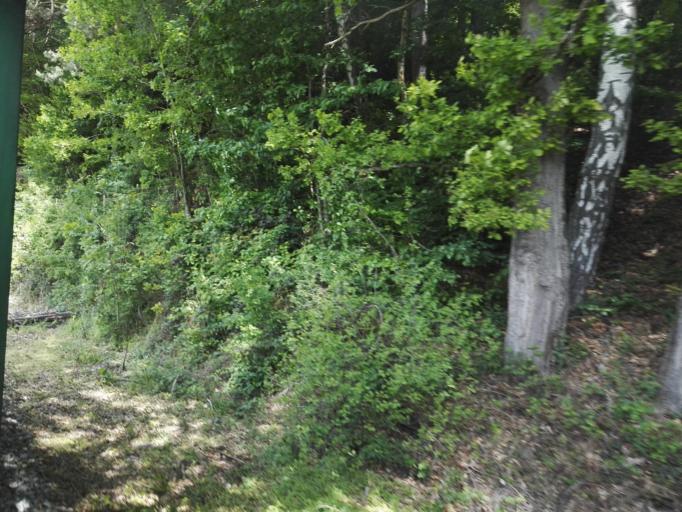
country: AT
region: Styria
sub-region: Politischer Bezirk Weiz
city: Anger
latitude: 47.2654
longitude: 15.7090
